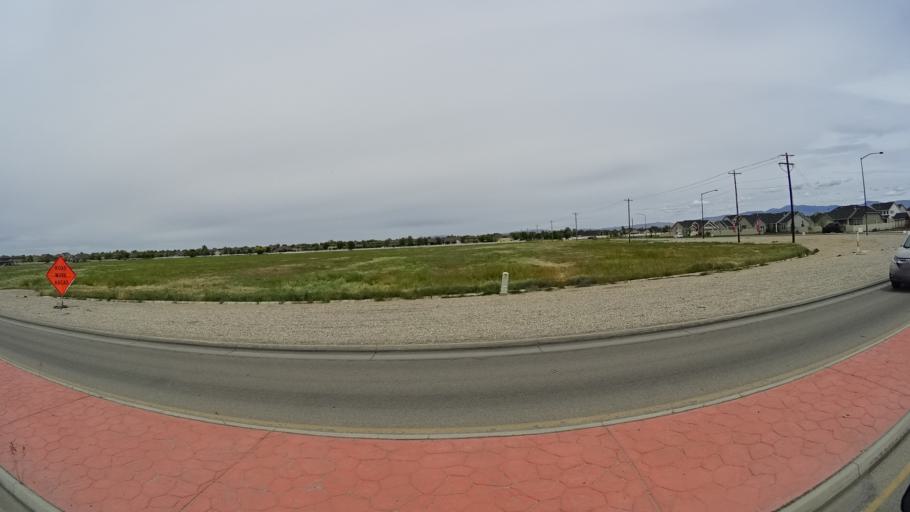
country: US
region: Idaho
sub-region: Ada County
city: Meridian
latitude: 43.5609
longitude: -116.3555
